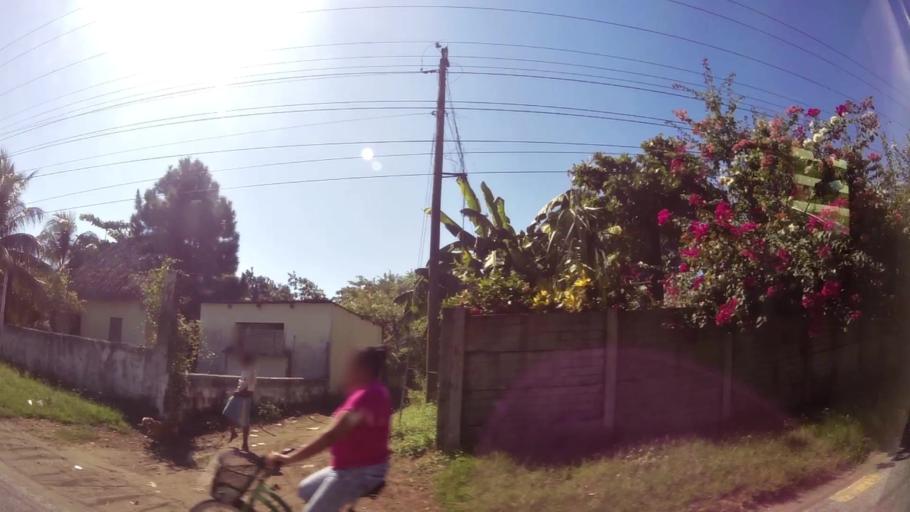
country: GT
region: Escuintla
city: Iztapa
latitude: 13.9188
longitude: -90.5567
